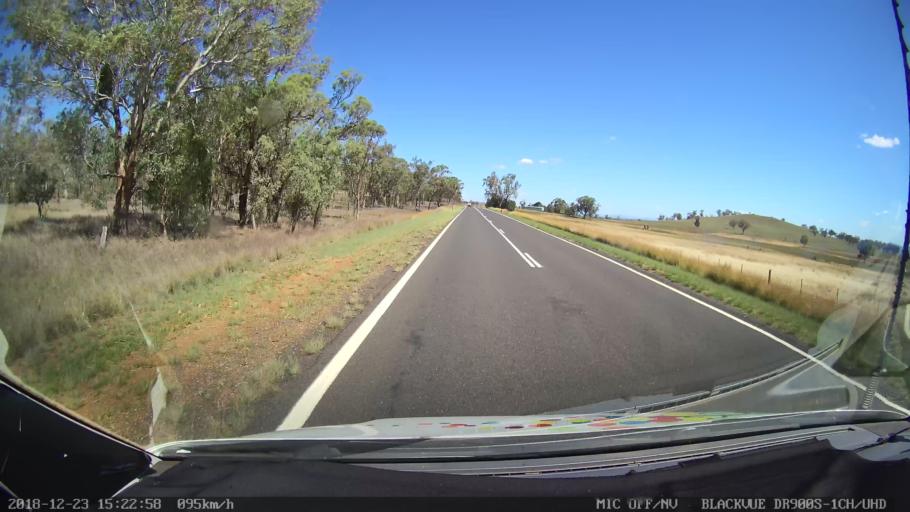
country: AU
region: New South Wales
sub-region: Tamworth Municipality
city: Manilla
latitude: -30.8746
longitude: 150.8097
